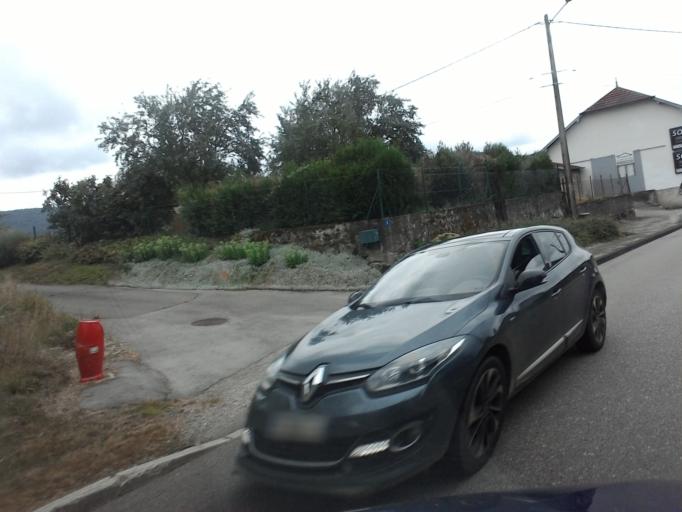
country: FR
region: Franche-Comte
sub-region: Departement du Doubs
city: Quingey
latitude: 47.0547
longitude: 5.8800
